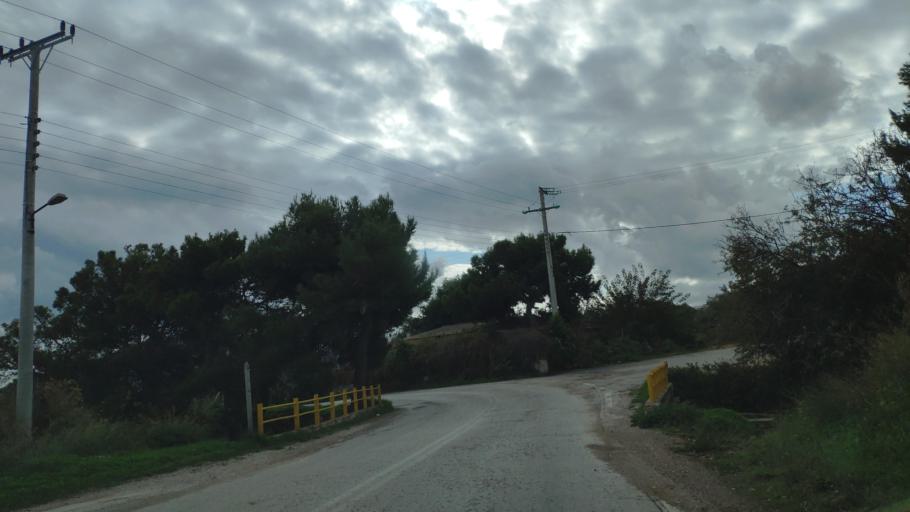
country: GR
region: Attica
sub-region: Nomarchia Anatolikis Attikis
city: Artemida
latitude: 37.9407
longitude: 24.0097
